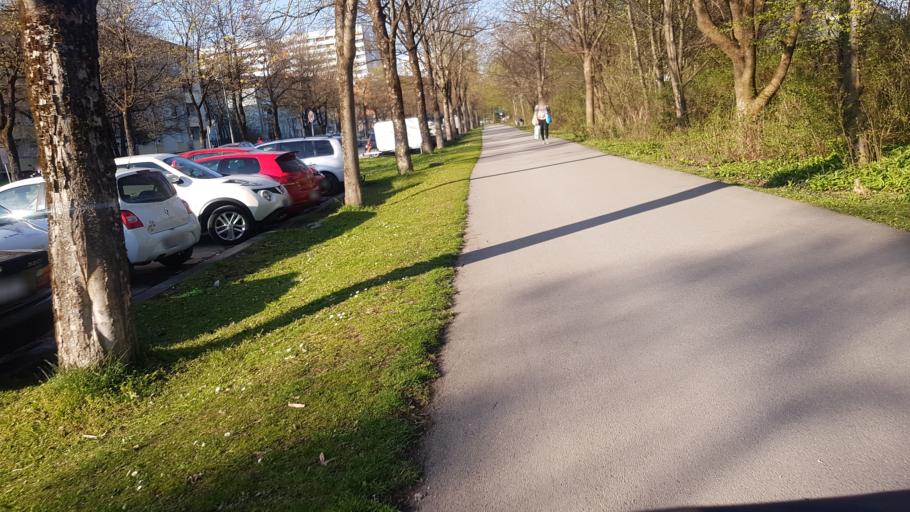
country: DE
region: Bavaria
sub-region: Upper Bavaria
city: Neuried
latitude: 48.0933
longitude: 11.4938
